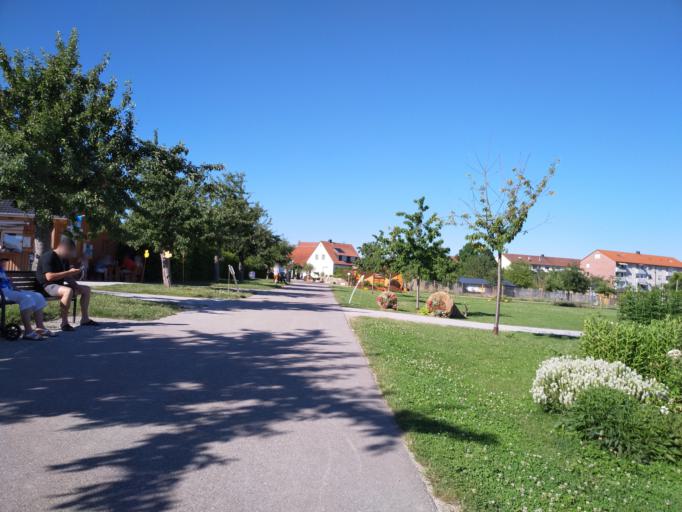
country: DE
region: Baden-Wuerttemberg
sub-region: Regierungsbezirk Stuttgart
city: Mutlangen
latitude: 48.8140
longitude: 9.7743
